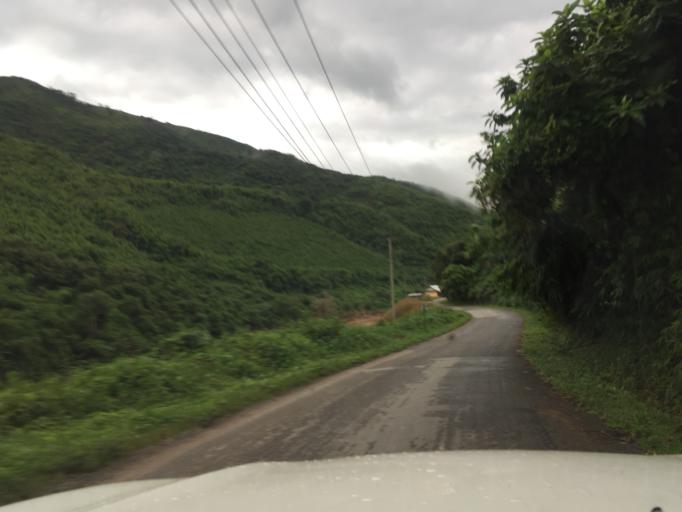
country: LA
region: Oudomxai
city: Muang La
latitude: 20.9623
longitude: 102.2205
